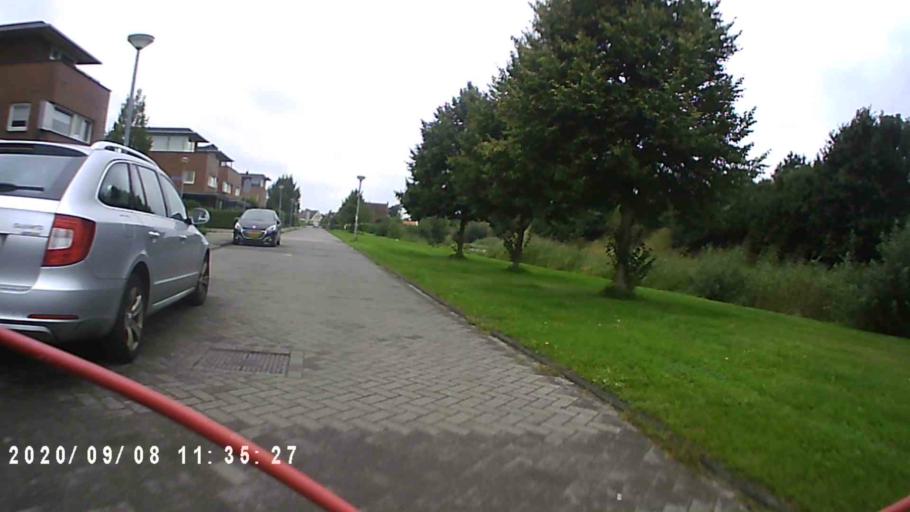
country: NL
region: Groningen
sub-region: Gemeente Hoogezand-Sappemeer
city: Sappemeer
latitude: 53.1579
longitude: 6.7812
